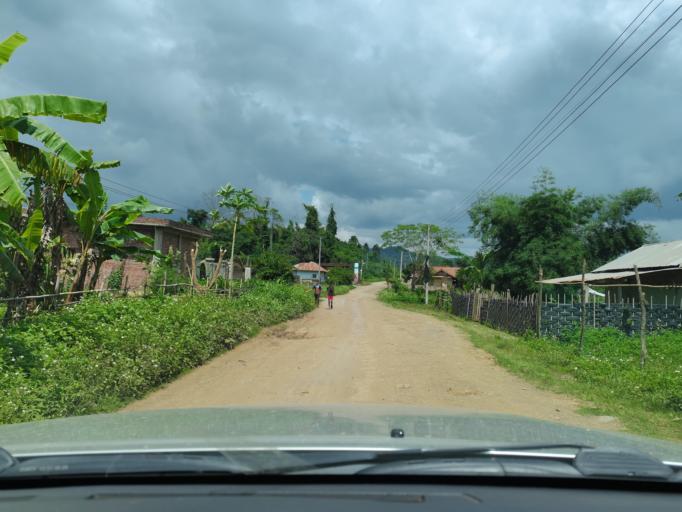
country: LA
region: Loungnamtha
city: Muang Long
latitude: 20.6810
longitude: 101.0537
